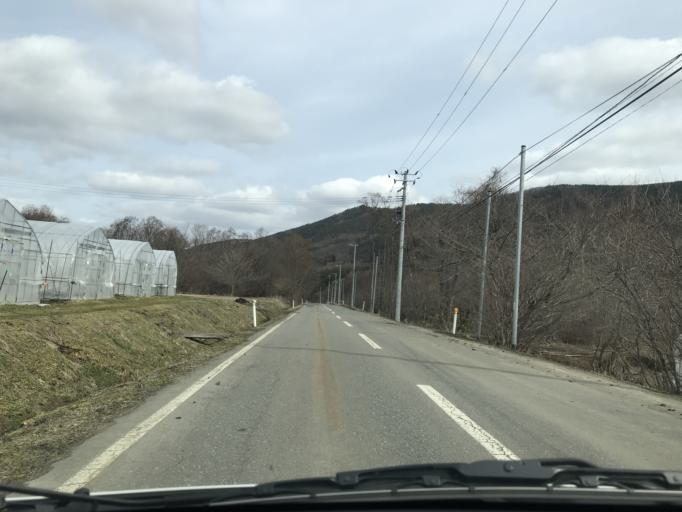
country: JP
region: Iwate
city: Kitakami
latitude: 39.2652
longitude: 141.3193
